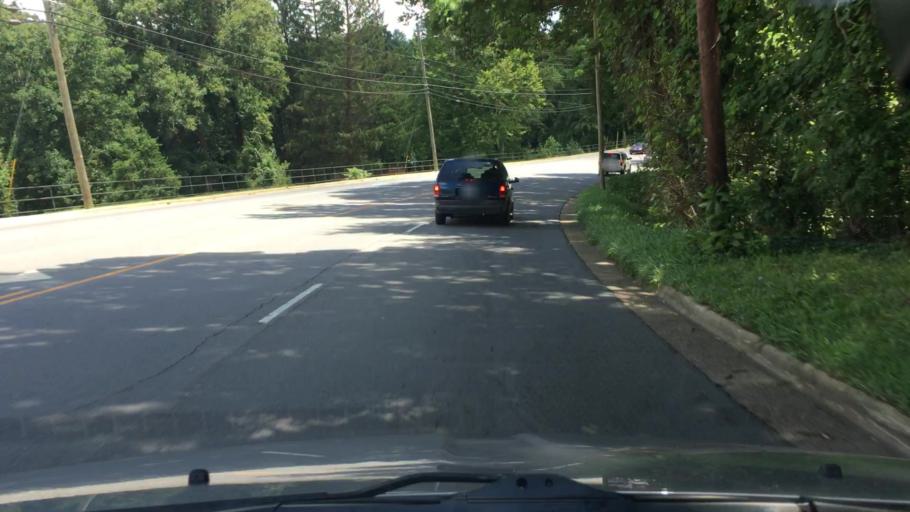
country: US
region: North Carolina
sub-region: Buncombe County
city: Asheville
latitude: 35.5898
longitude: -82.4985
